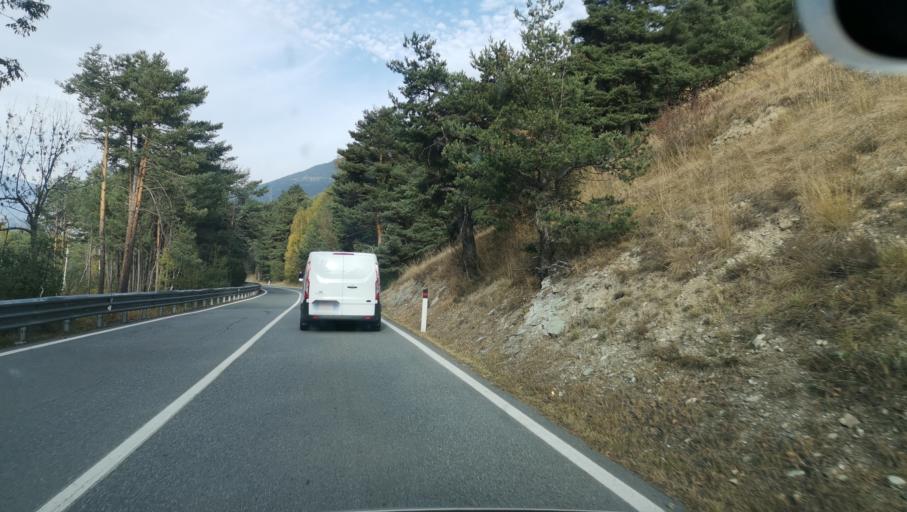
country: IT
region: Piedmont
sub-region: Provincia di Torino
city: Oulx
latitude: 45.0417
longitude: 6.8198
